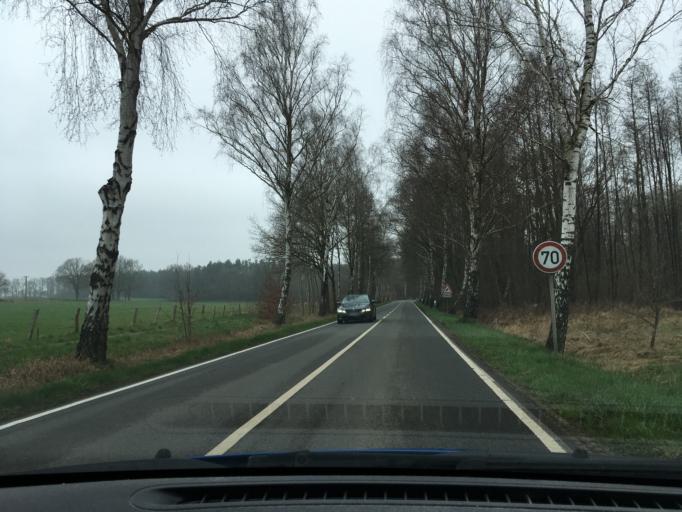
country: DE
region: Lower Saxony
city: Thomasburg
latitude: 53.2301
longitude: 10.6541
